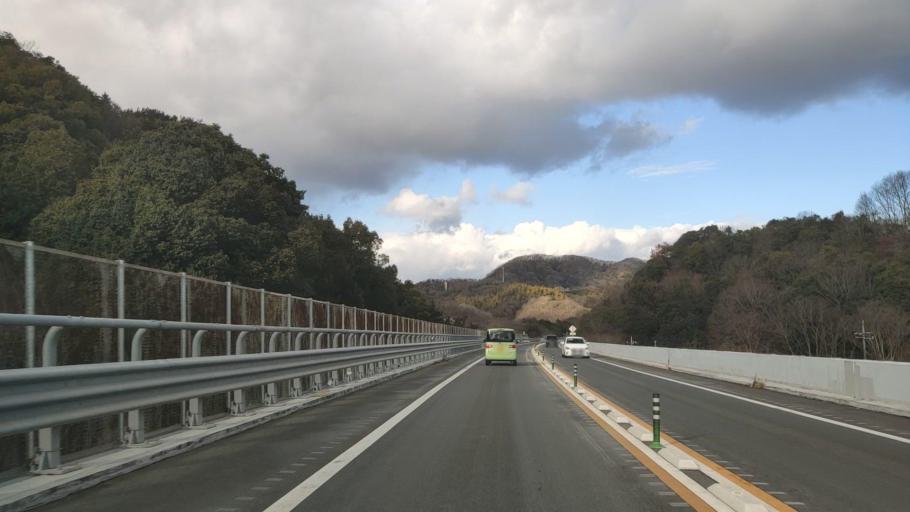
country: JP
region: Hiroshima
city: Onomichi
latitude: 34.3701
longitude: 133.1904
